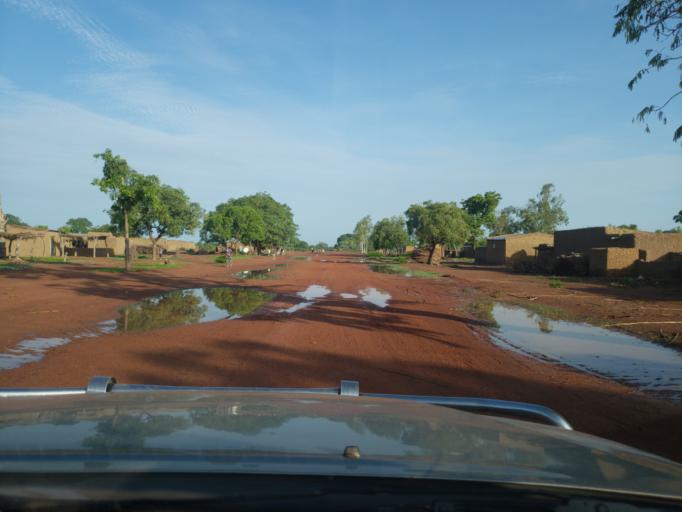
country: ML
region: Sikasso
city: Koutiala
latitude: 12.4186
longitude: -5.5770
